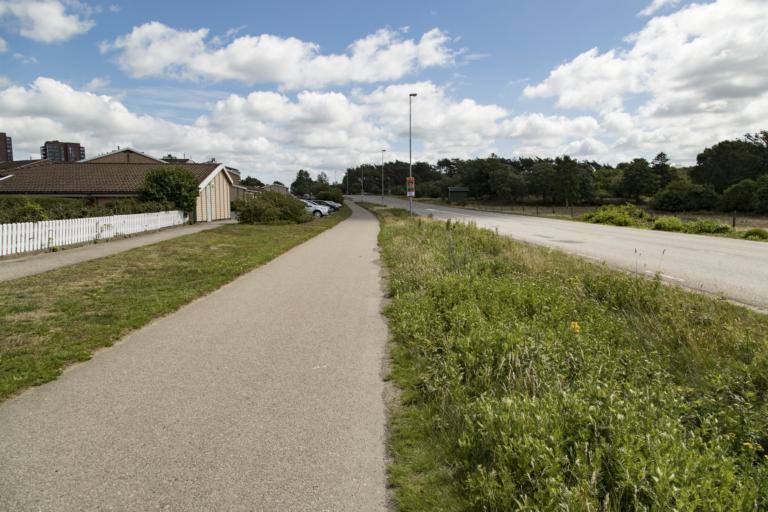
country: SE
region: Halland
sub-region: Varbergs Kommun
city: Varberg
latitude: 57.0893
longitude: 12.2577
